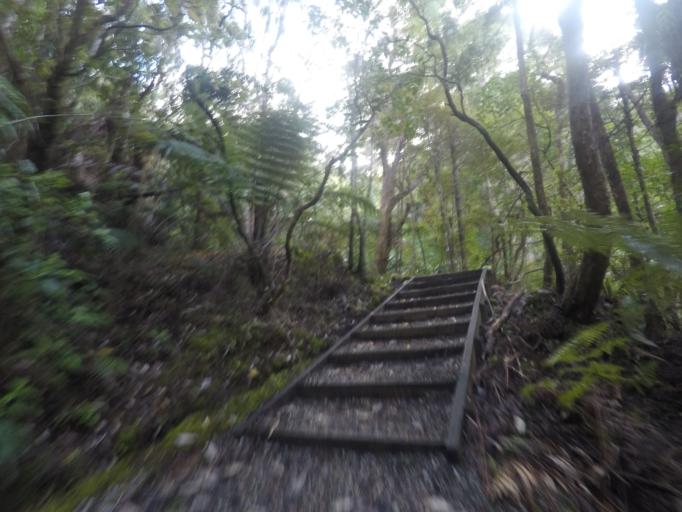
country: NZ
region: Auckland
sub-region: Auckland
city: Titirangi
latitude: -37.0028
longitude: 174.5550
